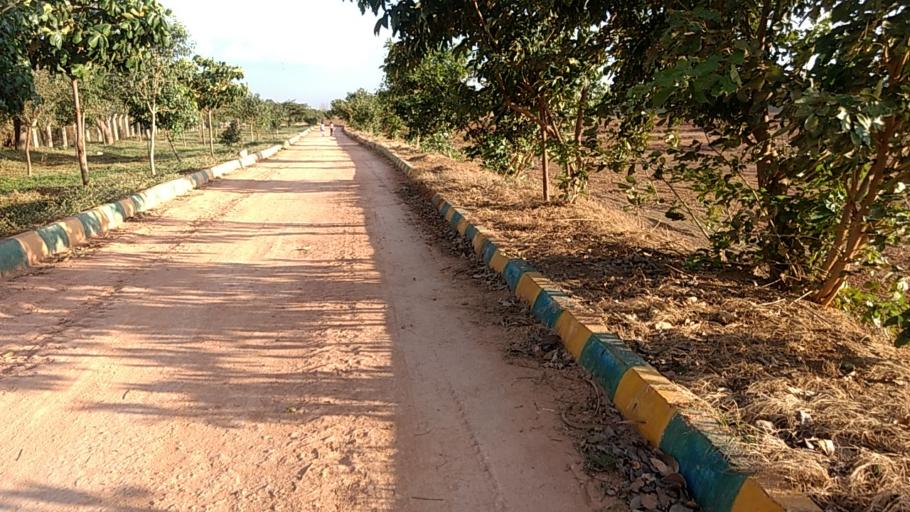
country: IN
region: Karnataka
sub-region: Bangalore Urban
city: Yelahanka
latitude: 13.0668
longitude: 77.5643
